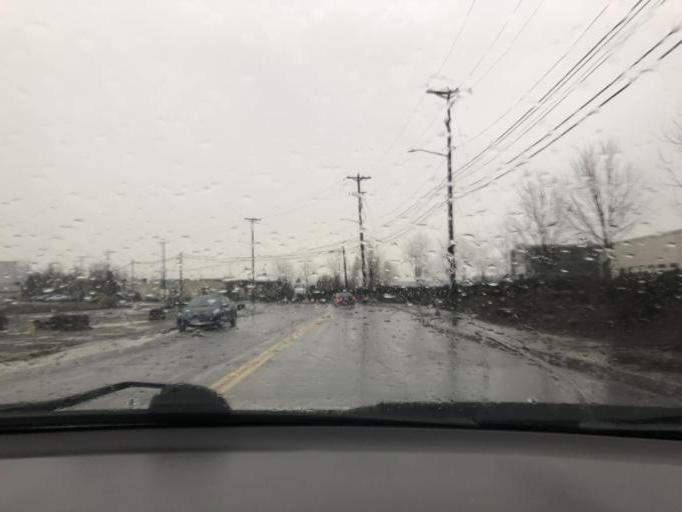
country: US
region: Washington
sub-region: Pierce County
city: Tacoma
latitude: 47.2527
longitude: -122.4237
